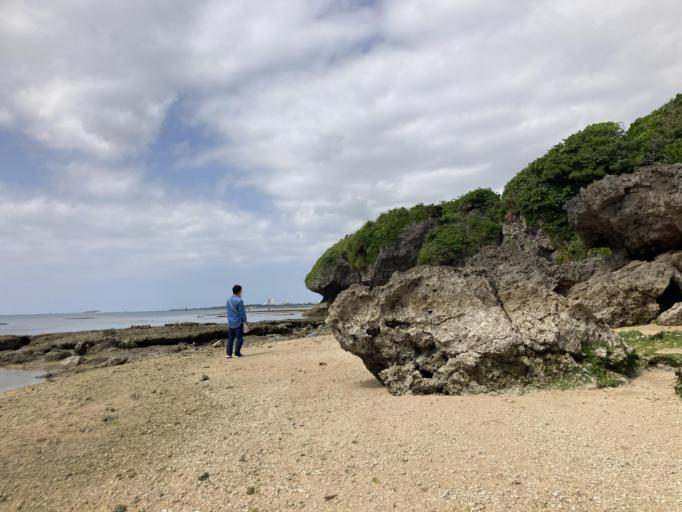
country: JP
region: Okinawa
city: Itoman
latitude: 26.1086
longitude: 127.6581
